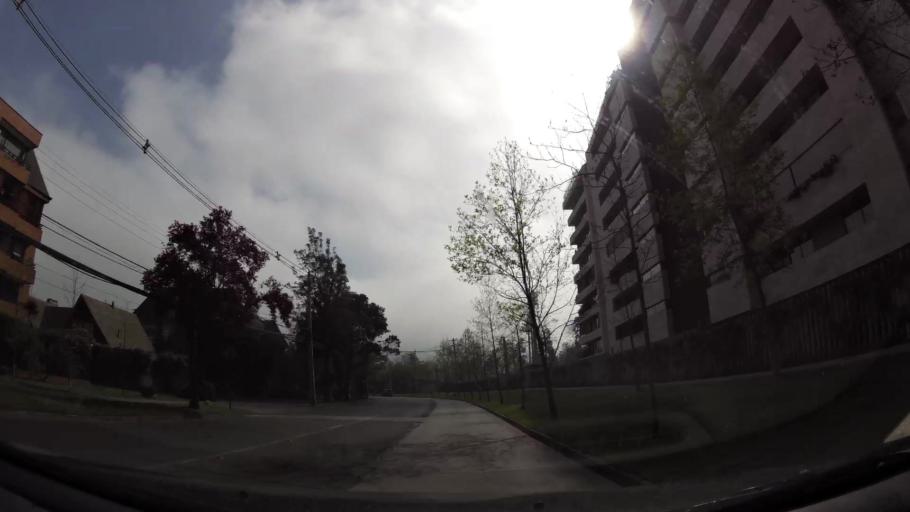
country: CL
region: Santiago Metropolitan
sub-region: Provincia de Santiago
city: Villa Presidente Frei, Nunoa, Santiago, Chile
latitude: -33.3822
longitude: -70.5690
